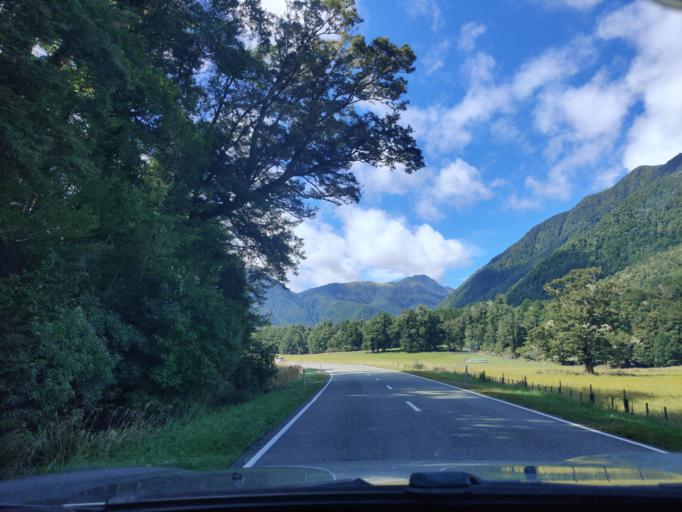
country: NZ
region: West Coast
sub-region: Buller District
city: Westport
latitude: -42.3552
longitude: 172.2102
